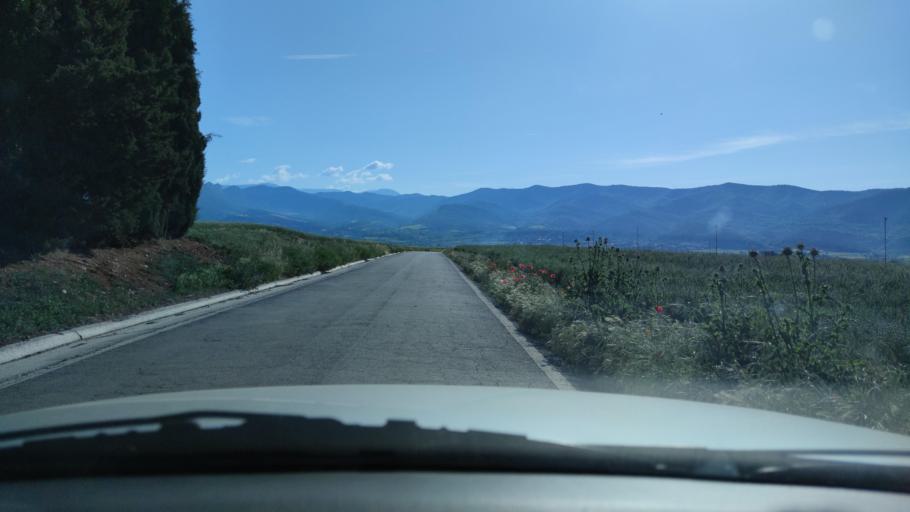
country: ES
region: Catalonia
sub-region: Provincia de Lleida
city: Oliana
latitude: 42.0640
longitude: 1.2810
